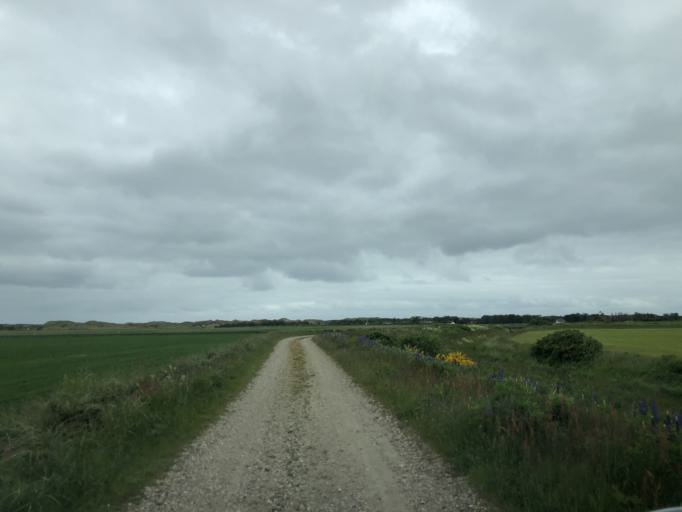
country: DK
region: Central Jutland
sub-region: Holstebro Kommune
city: Ulfborg
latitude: 56.2482
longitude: 8.1543
